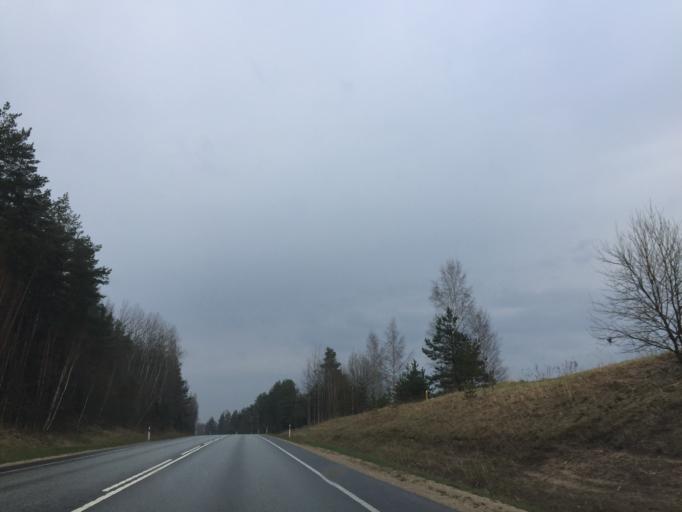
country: EE
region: Tartu
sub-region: UElenurme vald
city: Ulenurme
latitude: 58.1974
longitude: 26.7025
